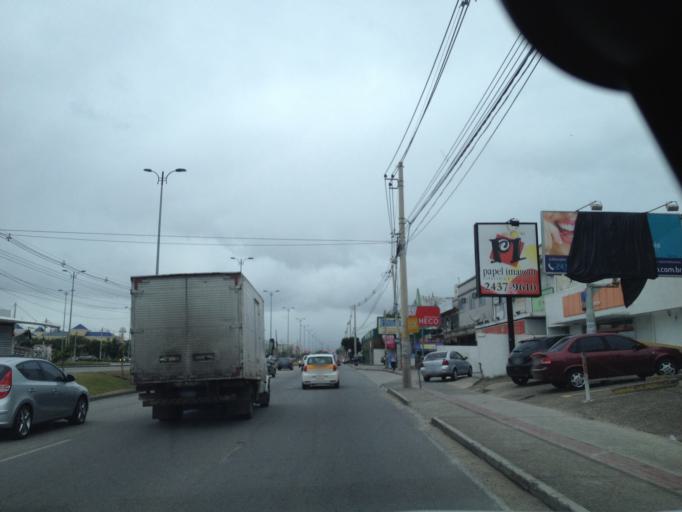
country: BR
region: Rio de Janeiro
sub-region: Nilopolis
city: Nilopolis
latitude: -23.0148
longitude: -43.4670
